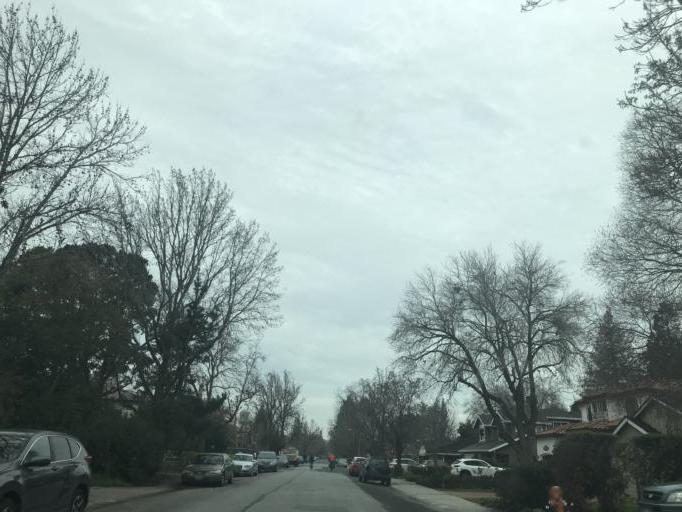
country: US
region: California
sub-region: Santa Clara County
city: Palo Alto
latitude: 37.4267
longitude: -122.1317
